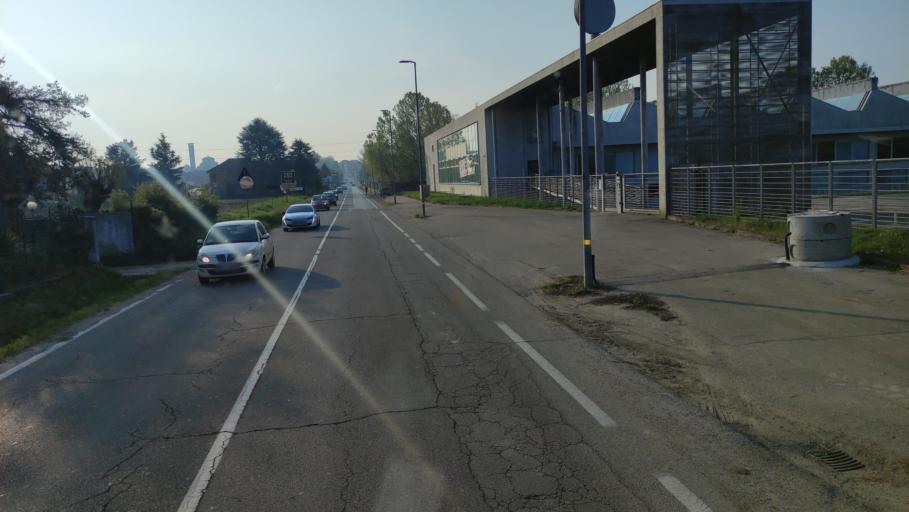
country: IT
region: Piedmont
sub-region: Provincia di Torino
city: Trofarello
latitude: 44.9891
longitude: 7.7230
